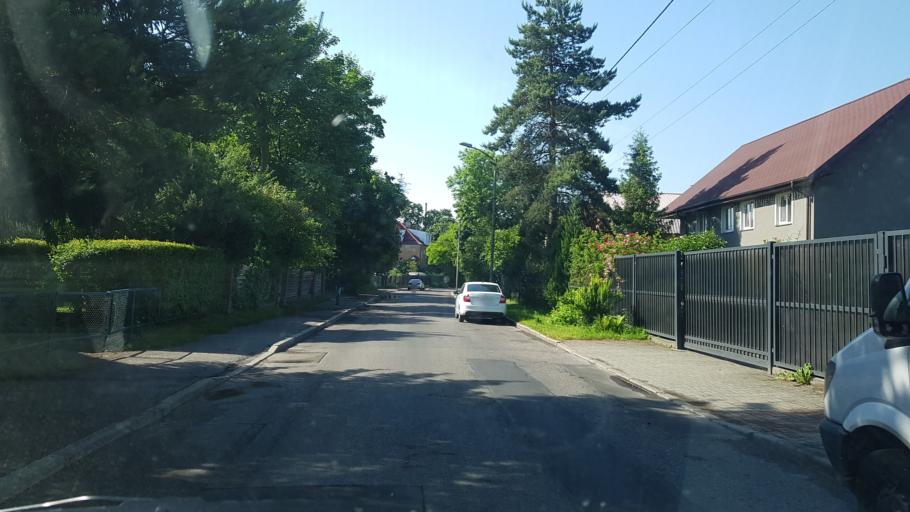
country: RU
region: Kaliningrad
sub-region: Gorod Kaliningrad
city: Kaliningrad
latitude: 54.7203
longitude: 20.4576
